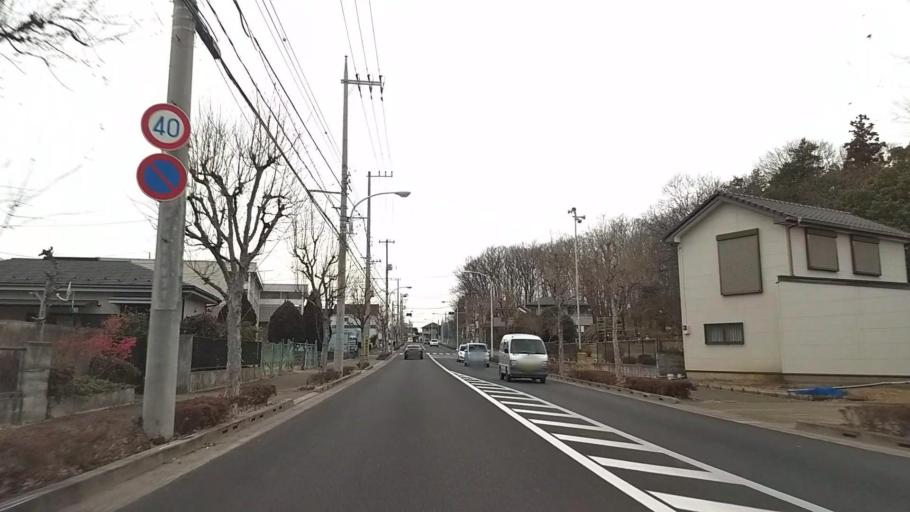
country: JP
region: Tokyo
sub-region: Machida-shi
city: Machida
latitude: 35.5218
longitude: 139.4624
